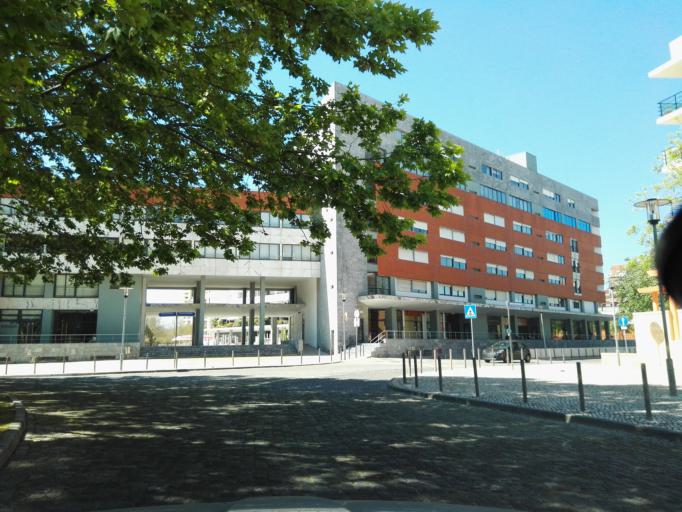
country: PT
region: Lisbon
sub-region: Loures
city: Moscavide
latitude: 38.7835
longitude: -9.0943
